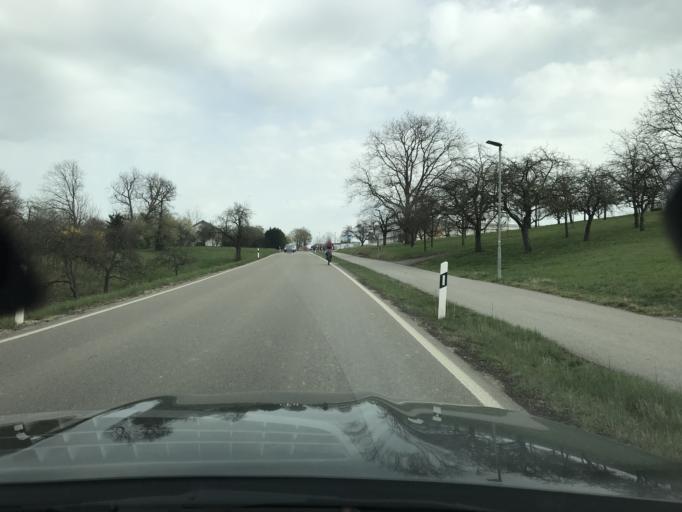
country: DE
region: Baden-Wuerttemberg
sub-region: Regierungsbezirk Stuttgart
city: Burgstetten
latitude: 48.9249
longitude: 9.3710
